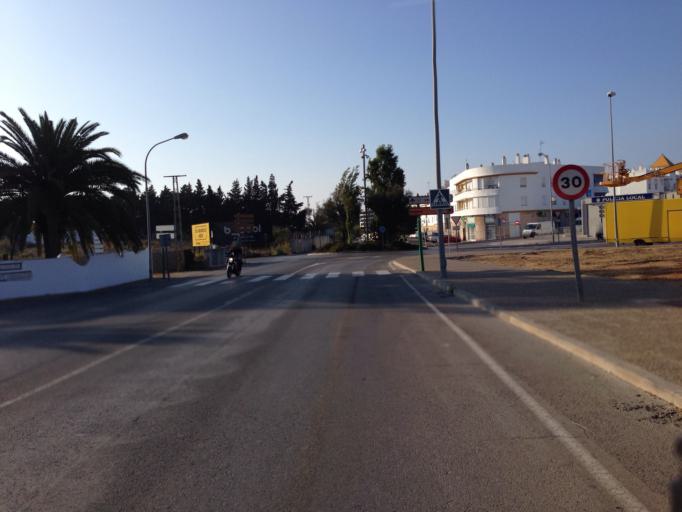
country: ES
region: Andalusia
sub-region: Provincia de Cadiz
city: Conil de la Frontera
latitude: 36.2843
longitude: -6.0915
